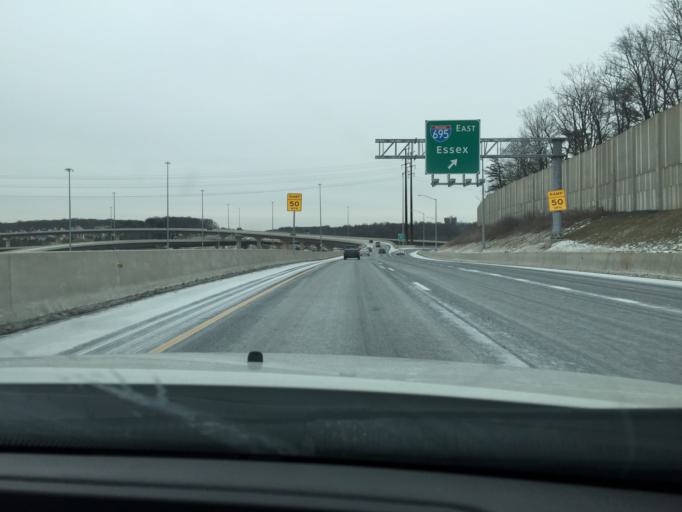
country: US
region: Maryland
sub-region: Baltimore County
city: Rossville
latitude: 39.3481
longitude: -76.5018
